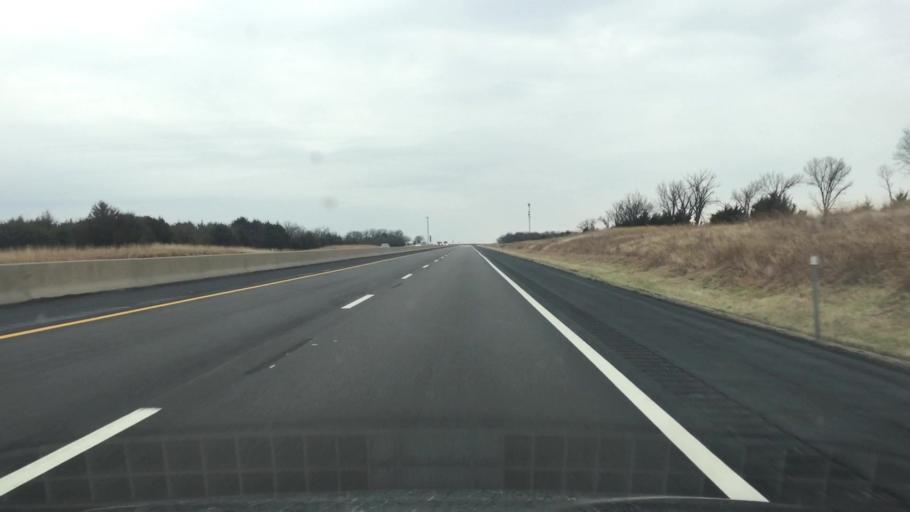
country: US
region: Kansas
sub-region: Shawnee County
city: Auburn
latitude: 38.8505
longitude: -95.8620
